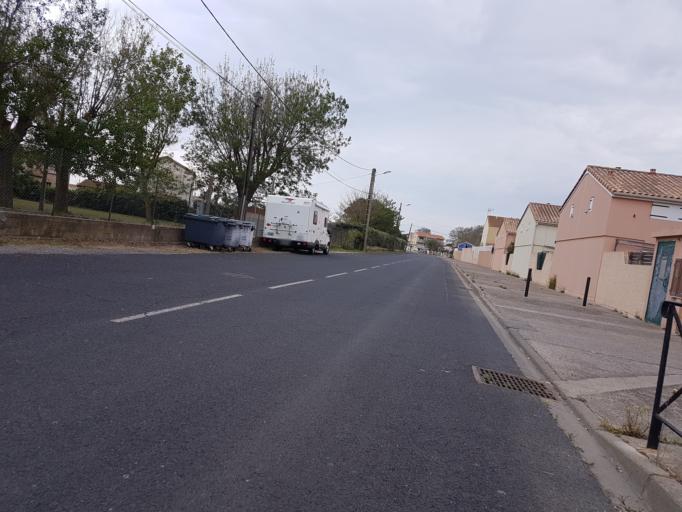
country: FR
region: Languedoc-Roussillon
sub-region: Departement de l'Herault
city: Marseillan
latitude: 43.3206
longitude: 3.5562
